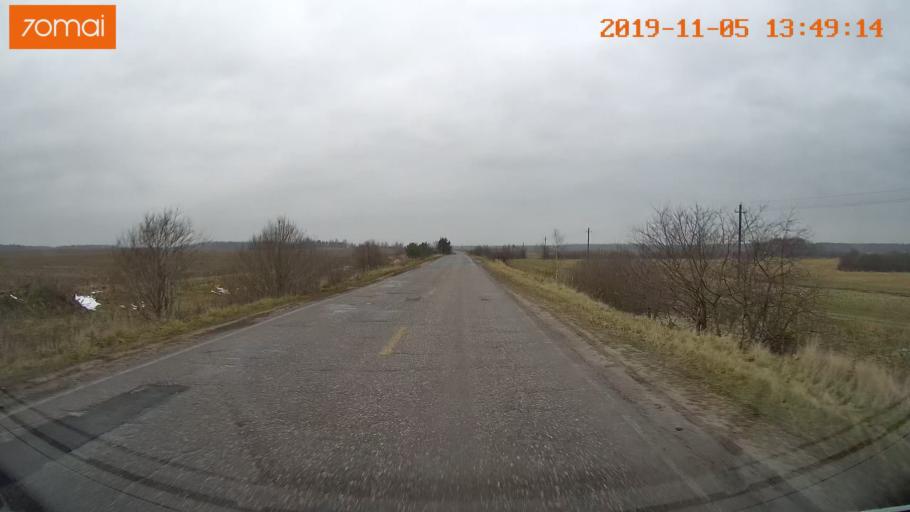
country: RU
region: Ivanovo
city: Kaminskiy
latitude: 57.0087
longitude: 41.4088
